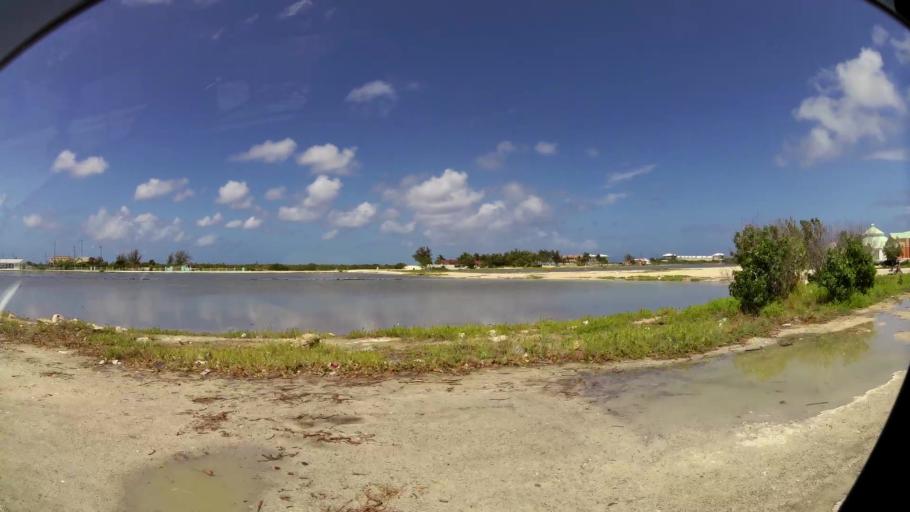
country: TC
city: Cockburn Town
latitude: 21.4801
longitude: -71.1457
